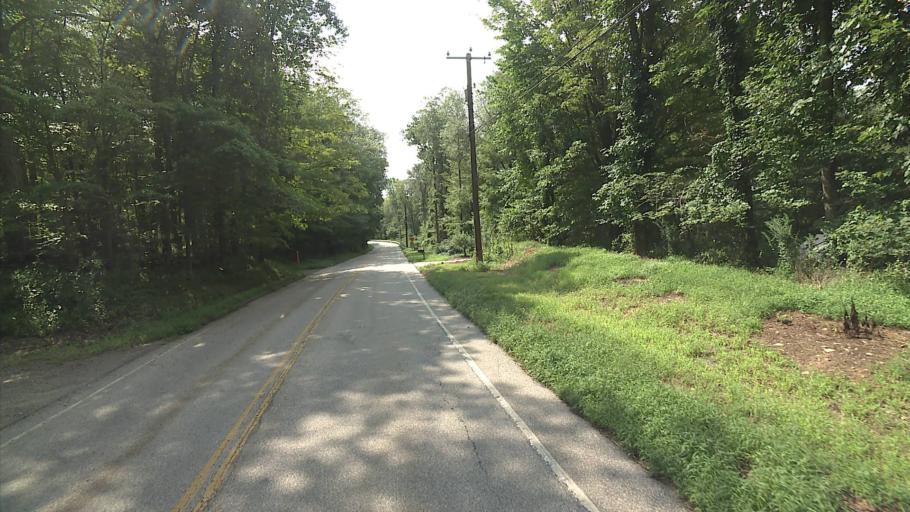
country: US
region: Connecticut
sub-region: Middlesex County
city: Chester Center
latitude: 41.4269
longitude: -72.4056
